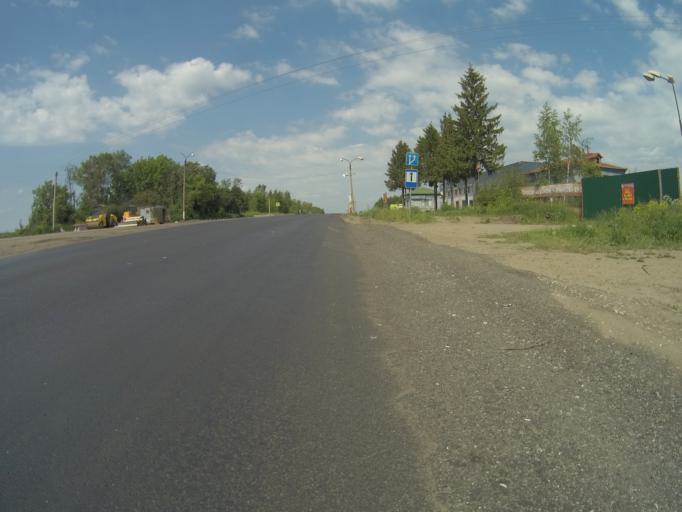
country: RU
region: Vladimir
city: Bogolyubovo
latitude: 56.2787
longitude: 40.4663
